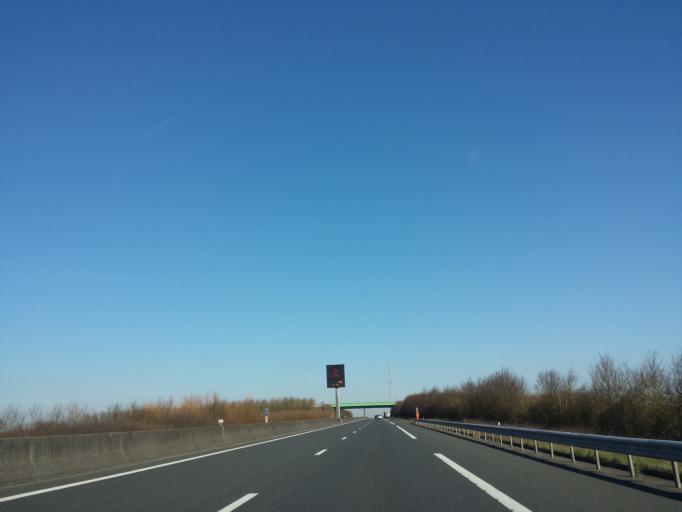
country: FR
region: Picardie
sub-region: Departement de l'Oise
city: Crevecoeur-le-Grand
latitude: 49.5532
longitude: 2.1912
